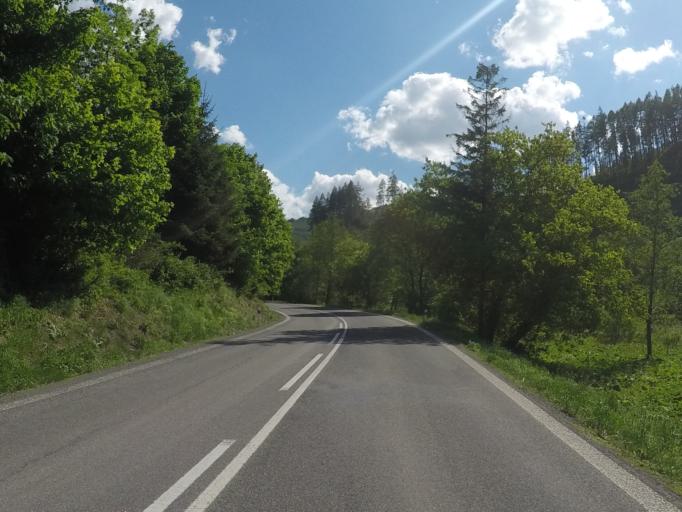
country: SK
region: Presovsky
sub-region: Okres Poprad
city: Poprad
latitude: 48.9691
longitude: 20.2948
